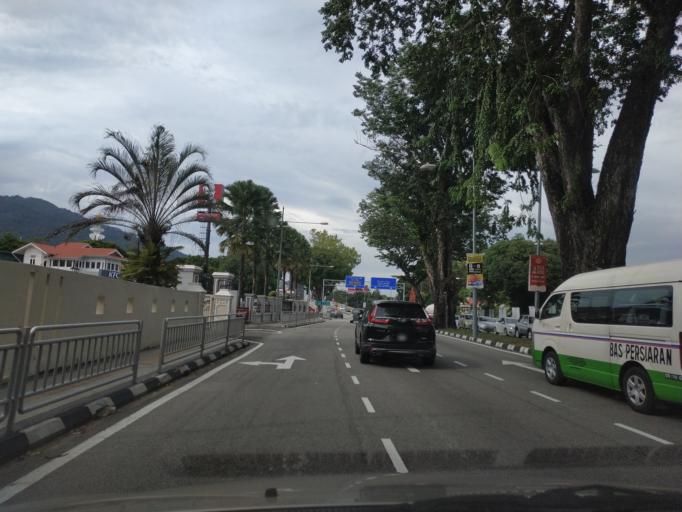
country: MY
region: Penang
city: George Town
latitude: 5.4045
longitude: 100.3036
